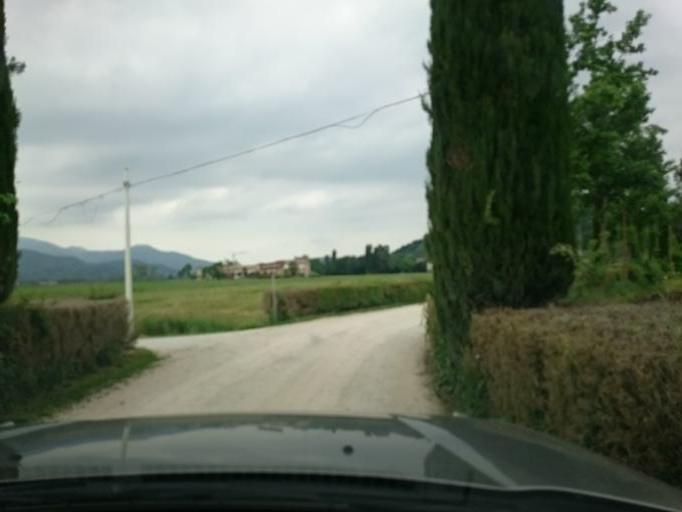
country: IT
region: Veneto
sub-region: Provincia di Padova
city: Battaglia Terme
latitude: 45.2762
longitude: 11.7647
